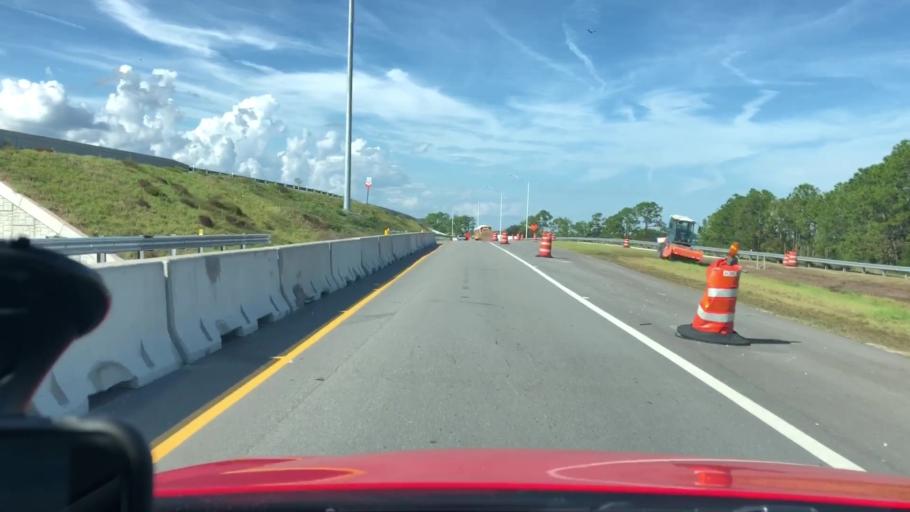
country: US
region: Florida
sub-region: Volusia County
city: South Daytona
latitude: 29.1575
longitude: -81.0764
